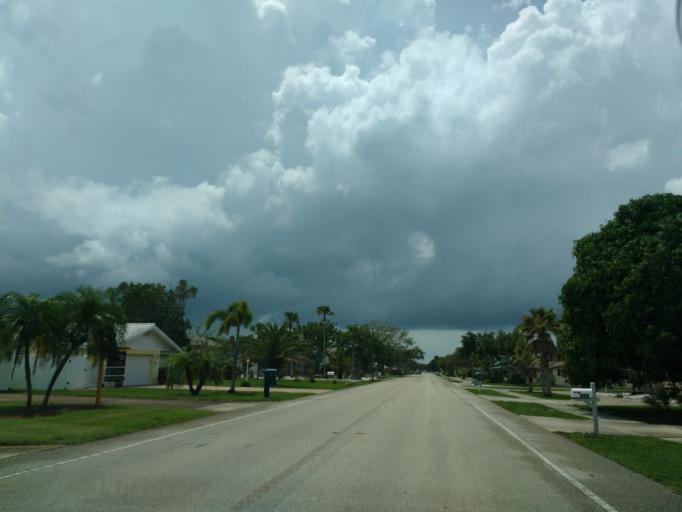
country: US
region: Florida
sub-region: Sarasota County
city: Venice
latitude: 27.0847
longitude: -82.4502
